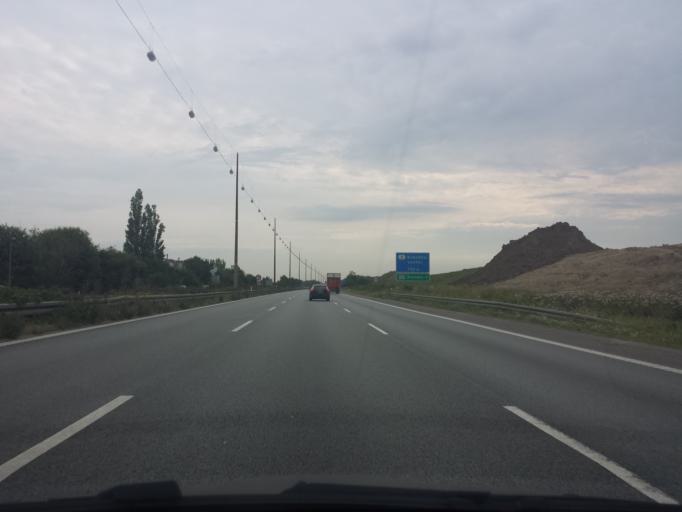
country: DK
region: Capital Region
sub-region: Vallensbaek Kommune
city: Vallensbaek
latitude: 55.6425
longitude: 12.3824
